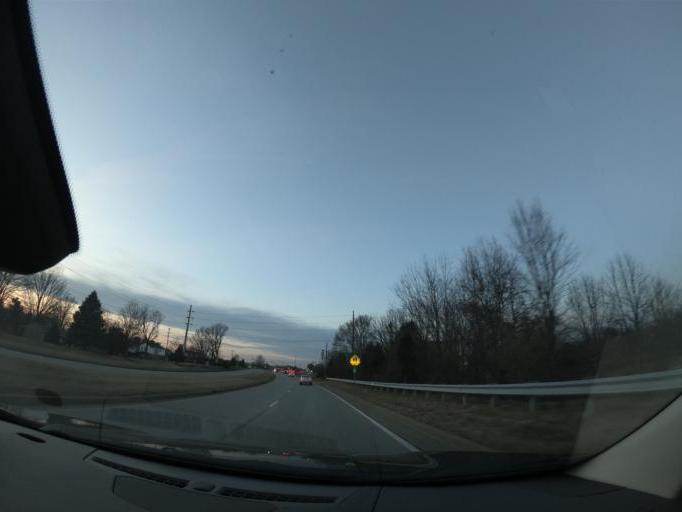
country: US
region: Kentucky
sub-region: Jefferson County
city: Worthington
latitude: 38.2844
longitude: -85.5691
